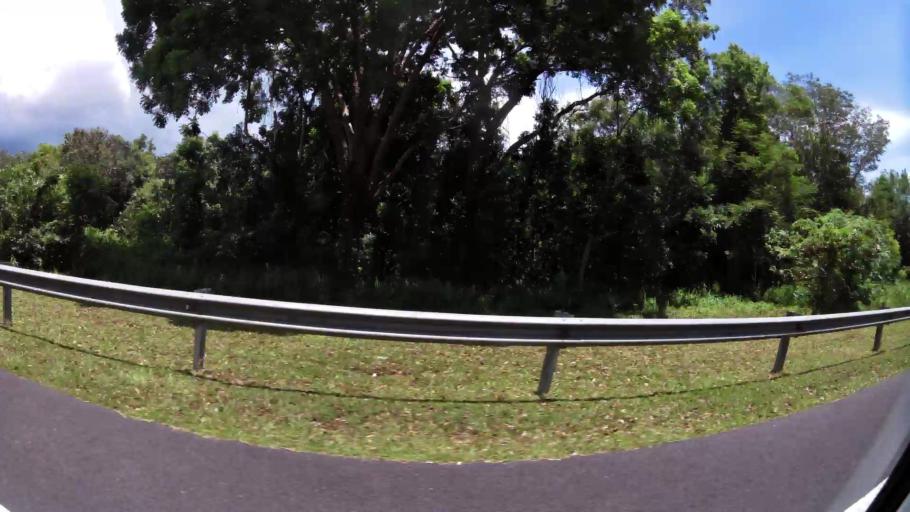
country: BN
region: Brunei and Muara
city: Bandar Seri Begawan
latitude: 4.9485
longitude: 114.9052
